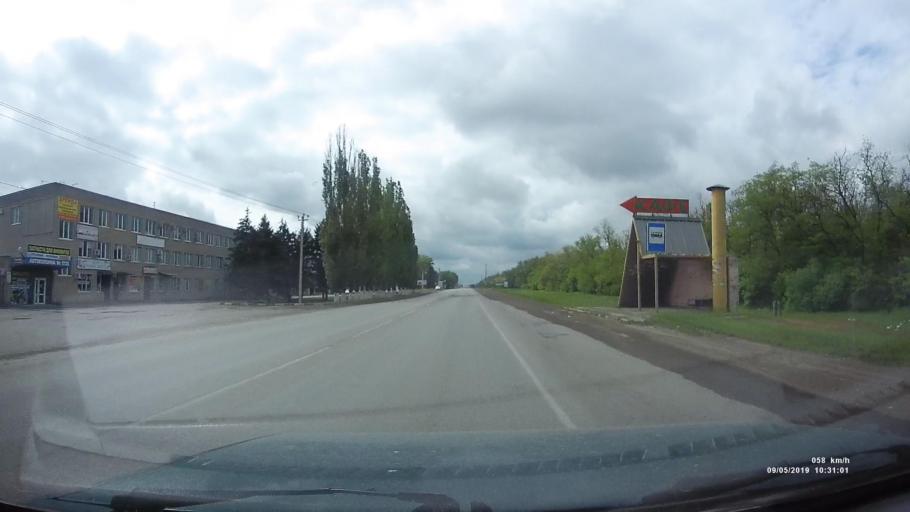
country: RU
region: Rostov
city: Azov
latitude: 47.0855
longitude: 39.4284
